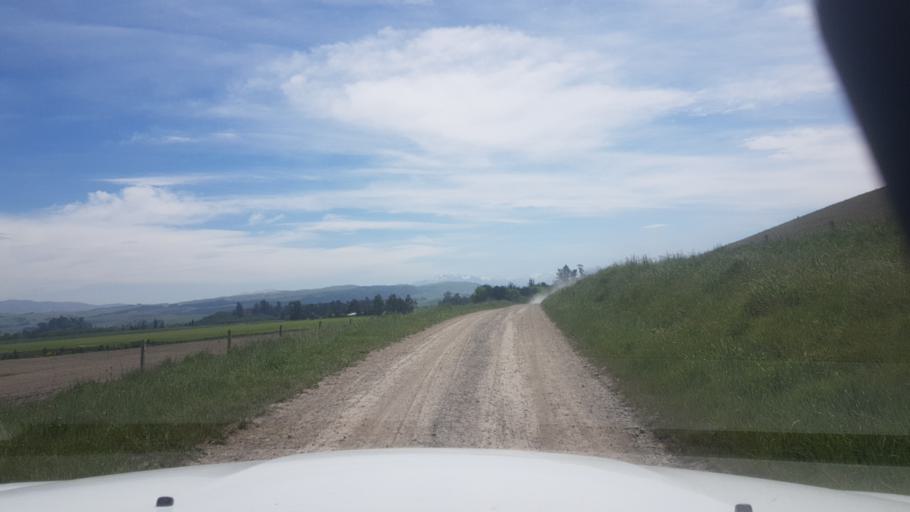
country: NZ
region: Canterbury
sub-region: Timaru District
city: Pleasant Point
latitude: -44.1700
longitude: 171.0179
